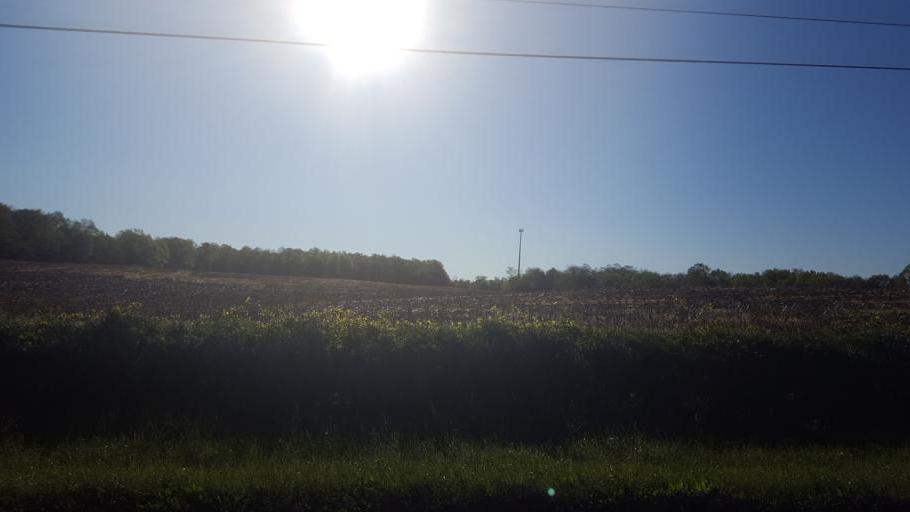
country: US
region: Ohio
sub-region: Delaware County
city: Sunbury
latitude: 40.2908
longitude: -82.8499
